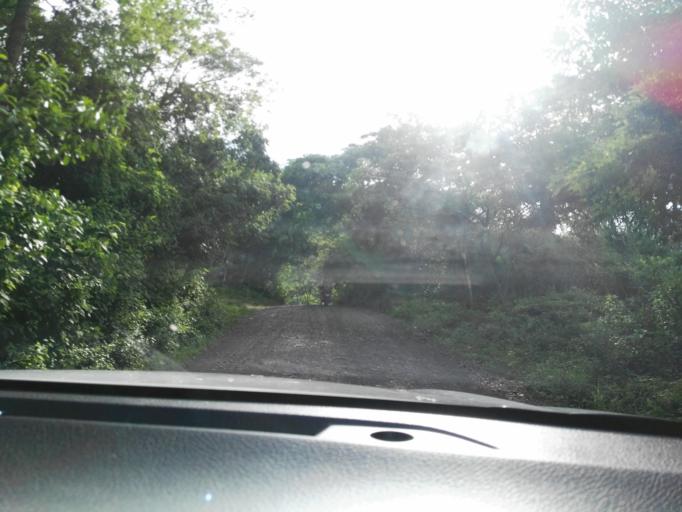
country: NI
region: Matagalpa
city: Terrabona
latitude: 12.8400
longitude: -86.0143
